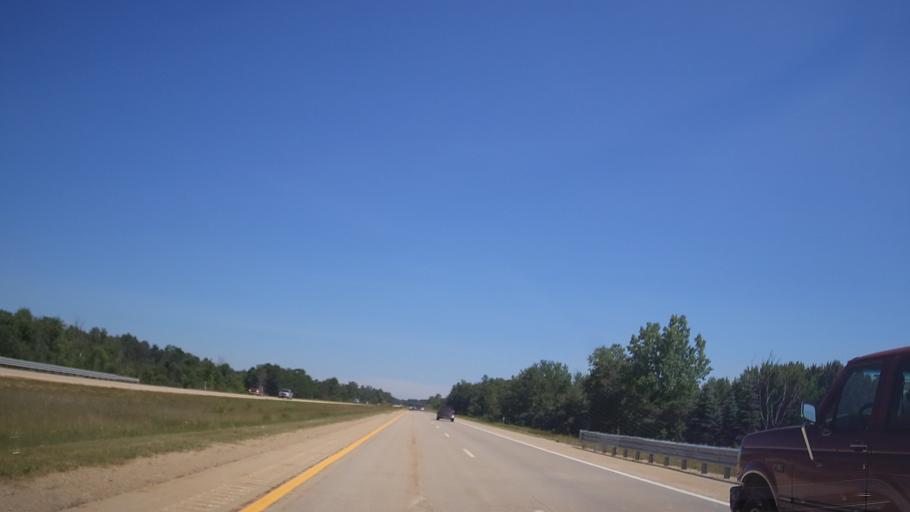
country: US
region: Michigan
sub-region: Midland County
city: Coleman
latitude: 43.7642
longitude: -84.5613
